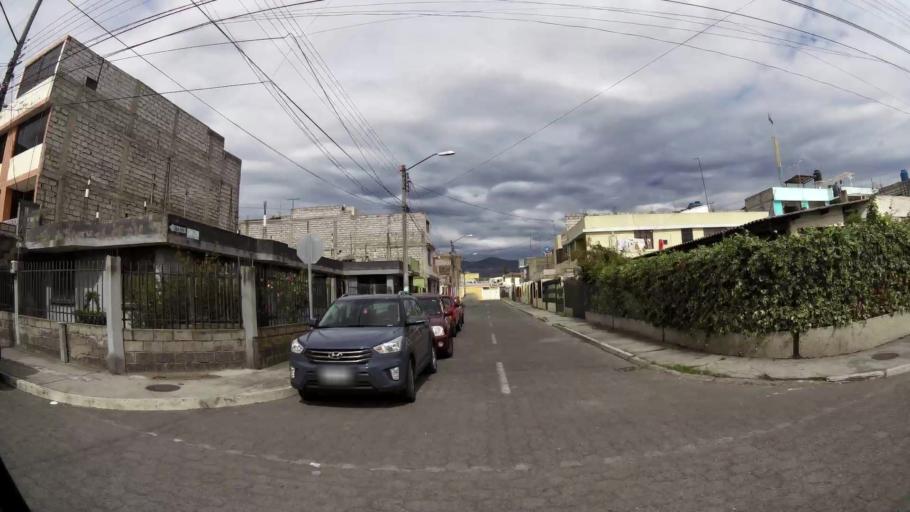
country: EC
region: Cotopaxi
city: Latacunga
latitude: -0.9238
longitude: -78.6225
